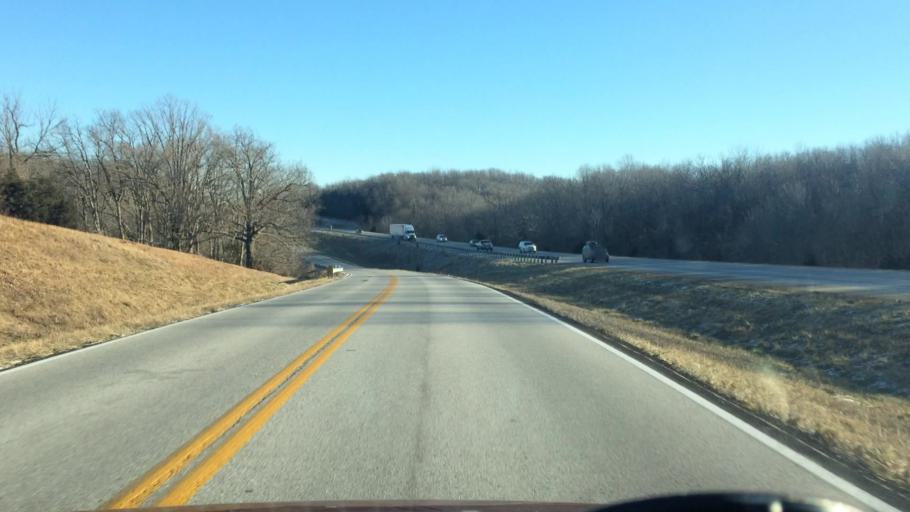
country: US
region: Missouri
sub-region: Greene County
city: Strafford
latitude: 37.2748
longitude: -93.0502
